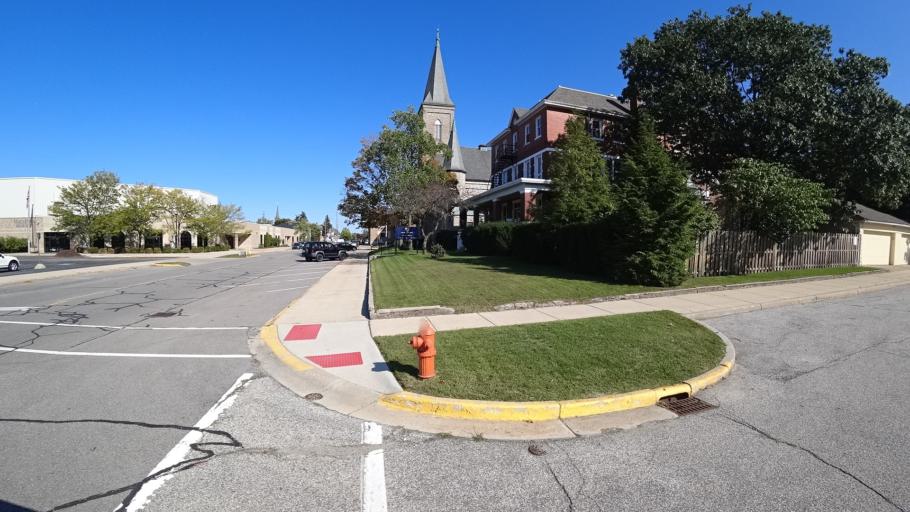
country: US
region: Indiana
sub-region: LaPorte County
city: Michigan City
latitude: 41.7106
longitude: -86.9044
